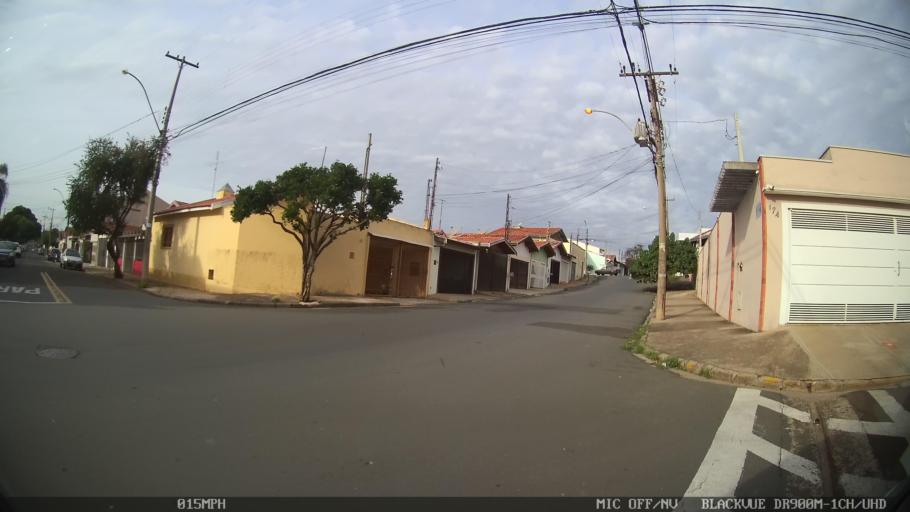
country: BR
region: Sao Paulo
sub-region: Piracicaba
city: Piracicaba
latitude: -22.7379
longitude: -47.6234
